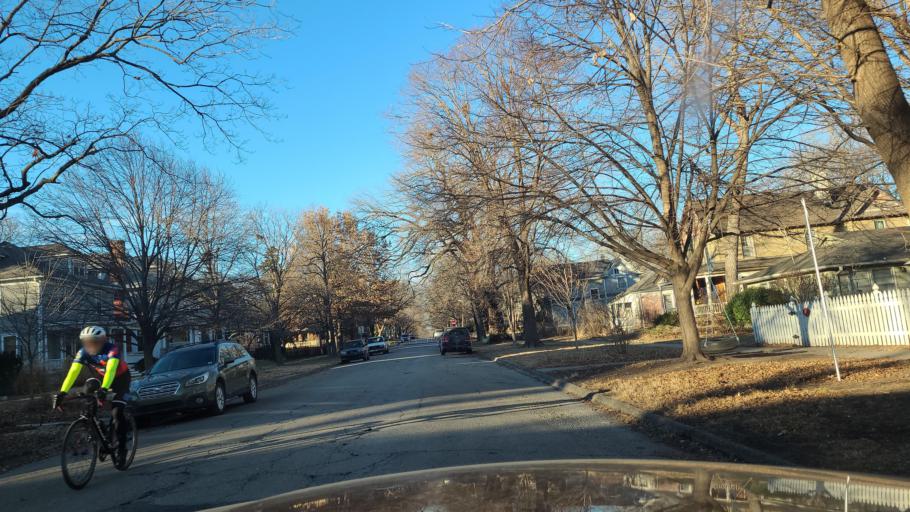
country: US
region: Kansas
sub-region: Douglas County
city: Lawrence
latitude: 38.9684
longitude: -95.2428
